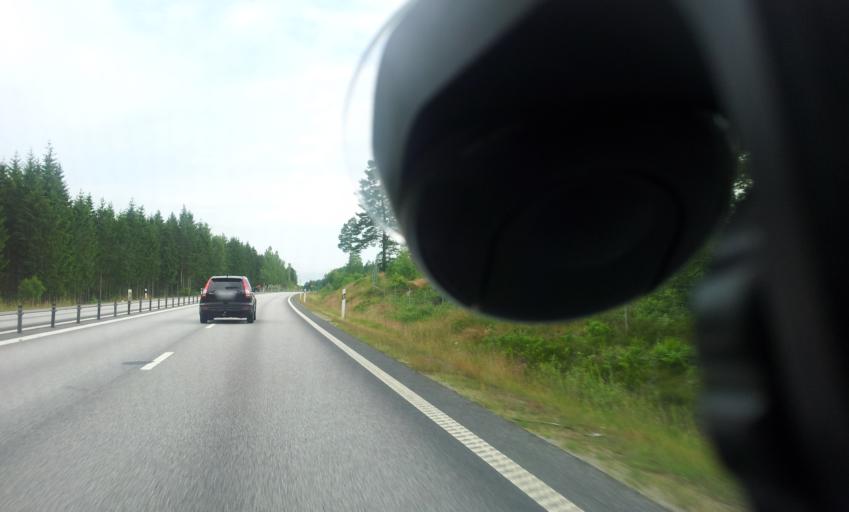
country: SE
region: OEstergoetland
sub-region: Valdemarsviks Kommun
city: Gusum
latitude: 58.2567
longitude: 16.5277
